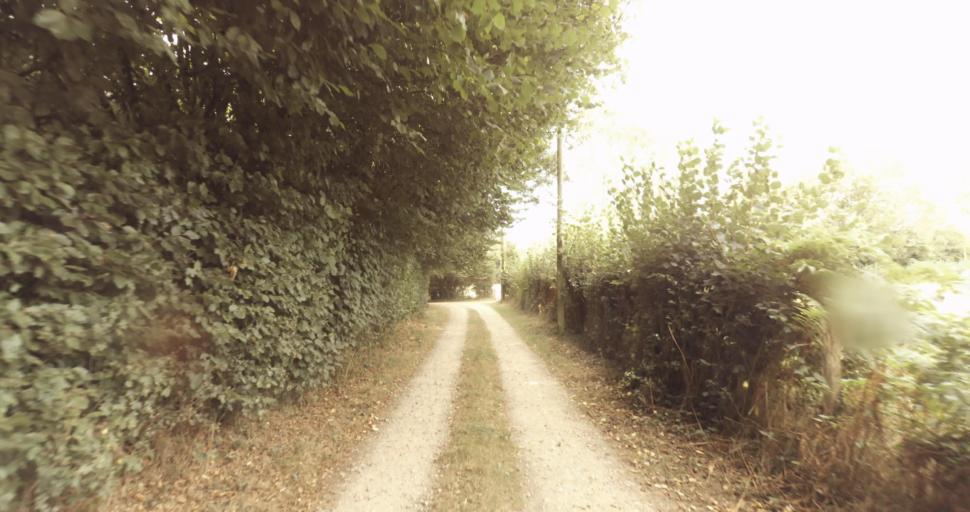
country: FR
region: Lower Normandy
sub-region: Departement de l'Orne
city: Vimoutiers
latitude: 48.9532
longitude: 0.3043
